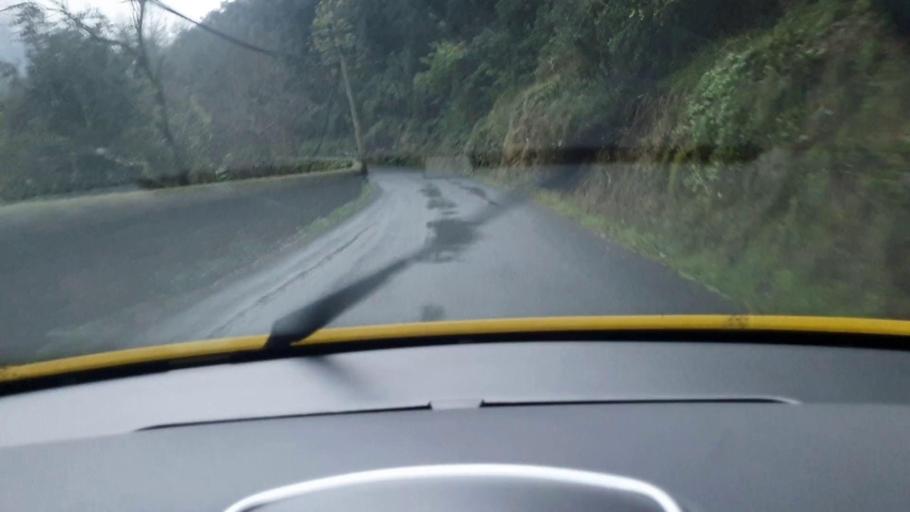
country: FR
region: Languedoc-Roussillon
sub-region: Departement du Gard
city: Sumene
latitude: 43.9895
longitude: 3.7124
